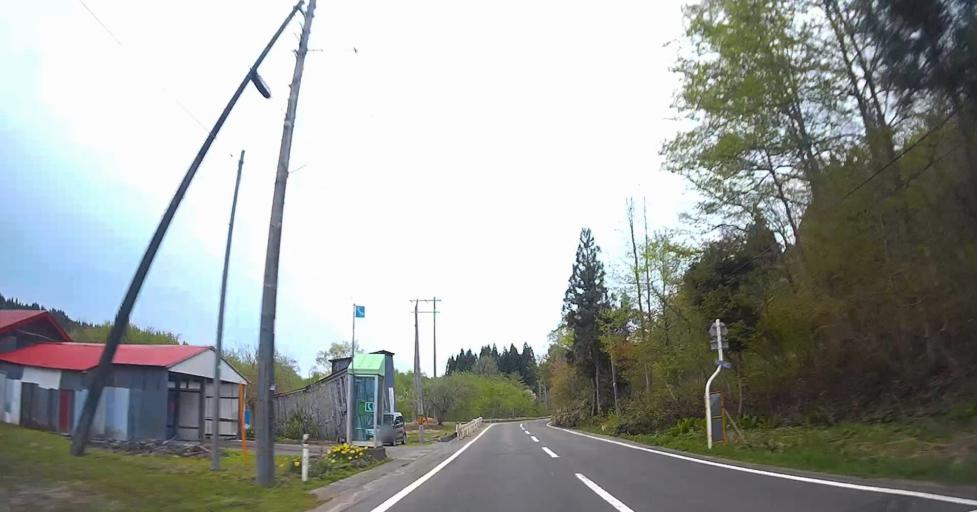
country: JP
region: Aomori
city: Goshogawara
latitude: 41.1289
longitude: 140.5198
